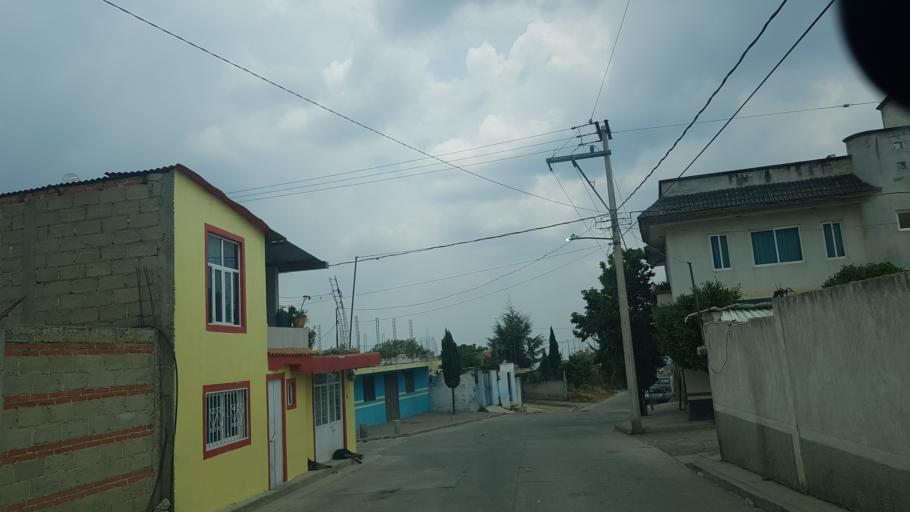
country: MX
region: Puebla
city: Domingo Arenas
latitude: 19.1520
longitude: -98.4906
